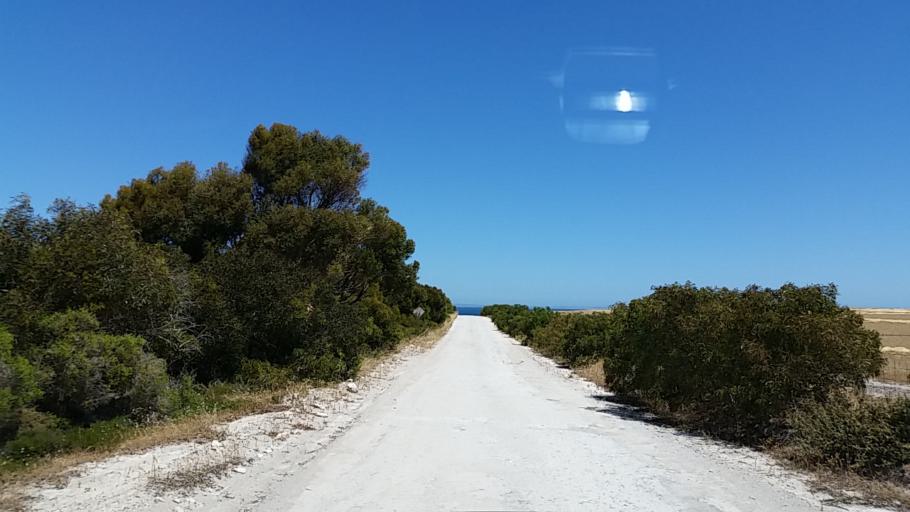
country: AU
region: South Australia
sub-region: Yorke Peninsula
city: Honiton
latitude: -35.2329
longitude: 137.1634
